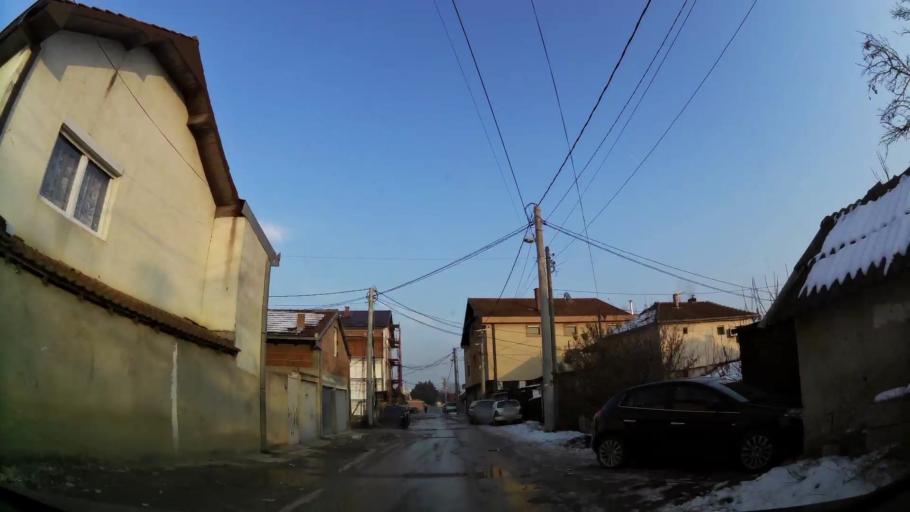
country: MK
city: Creshevo
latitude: 42.0147
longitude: 21.5177
